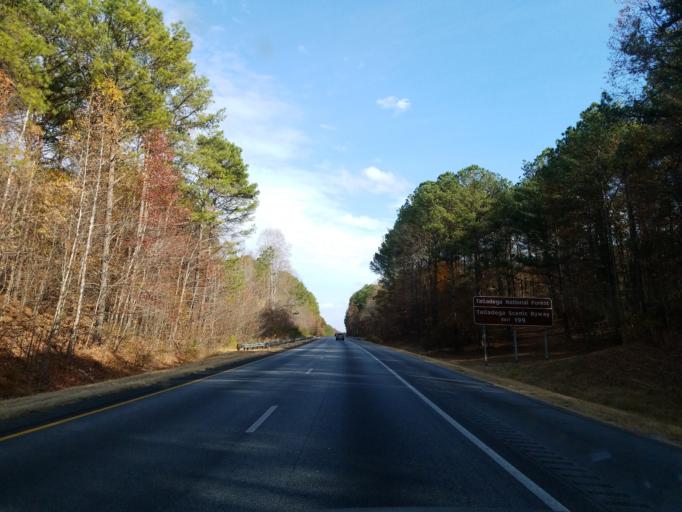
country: US
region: Alabama
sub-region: Cleburne County
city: Heflin
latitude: 33.6185
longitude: -85.6379
